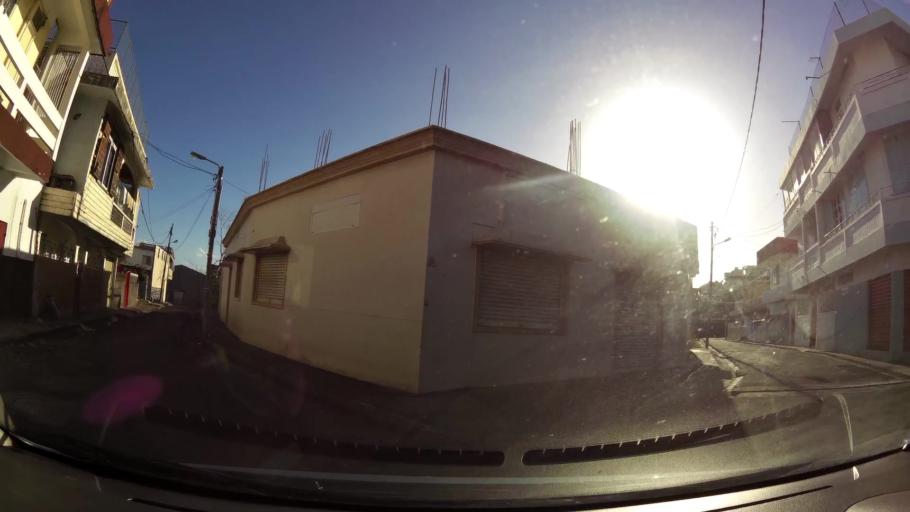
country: MU
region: Port Louis
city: Port Louis
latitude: -20.1550
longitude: 57.5069
